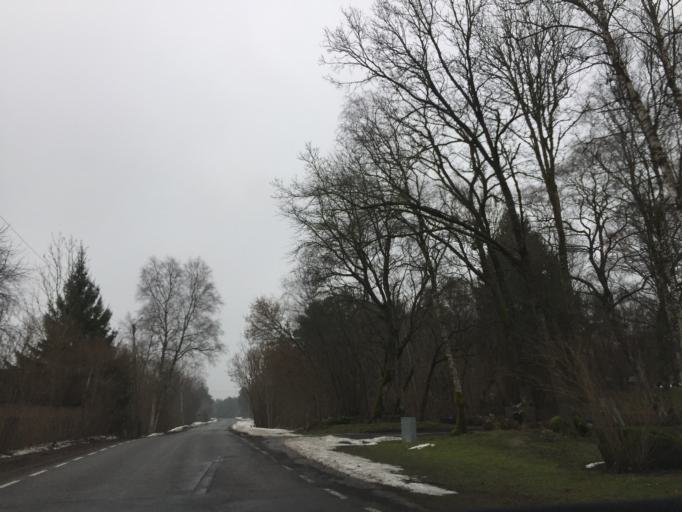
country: EE
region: Saare
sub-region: Orissaare vald
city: Orissaare
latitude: 58.4107
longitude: 22.8038
